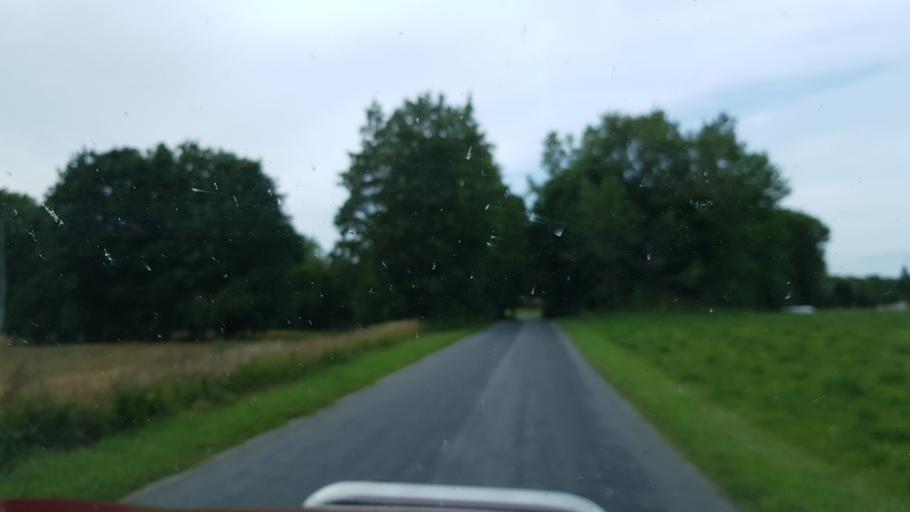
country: EE
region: Laeaene
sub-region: Ridala Parish
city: Uuemoisa
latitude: 59.0113
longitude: 23.7244
